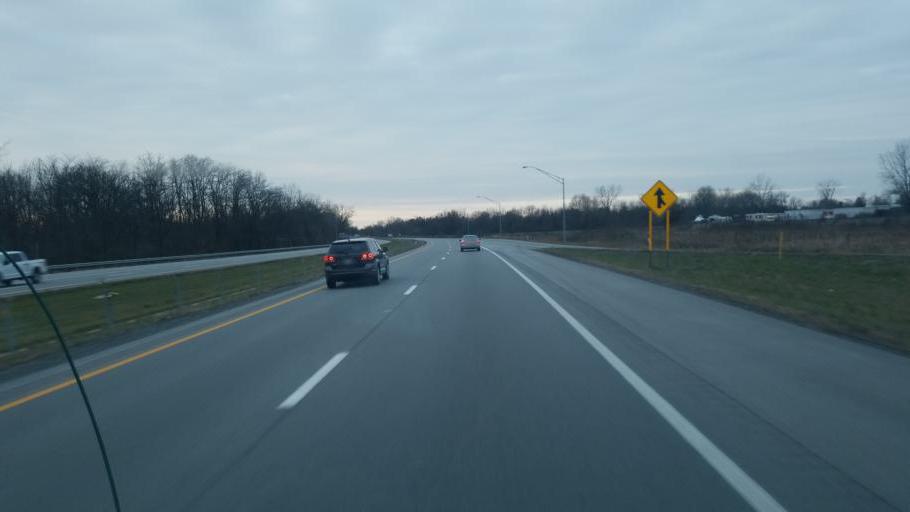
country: US
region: Ohio
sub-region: Allen County
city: Fort Shawnee
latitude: 40.6857
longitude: -84.1247
